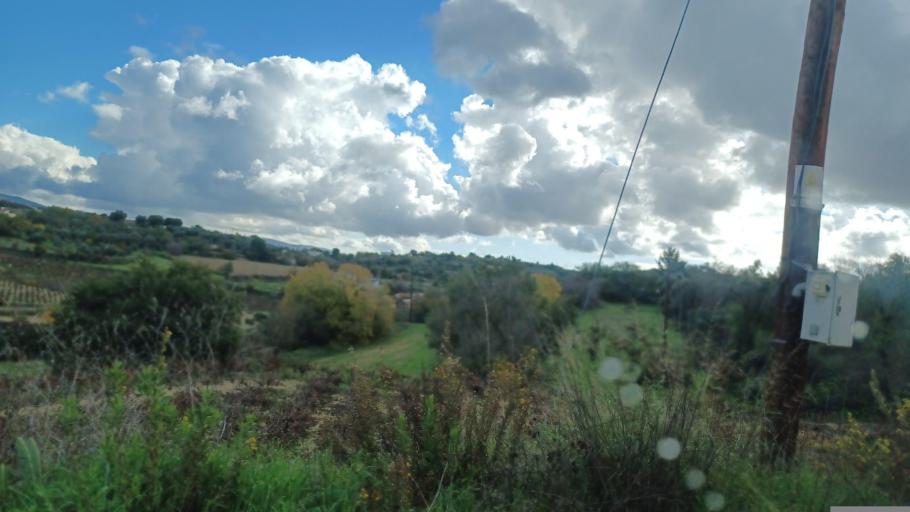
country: CY
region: Pafos
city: Mesogi
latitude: 34.8516
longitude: 32.5155
